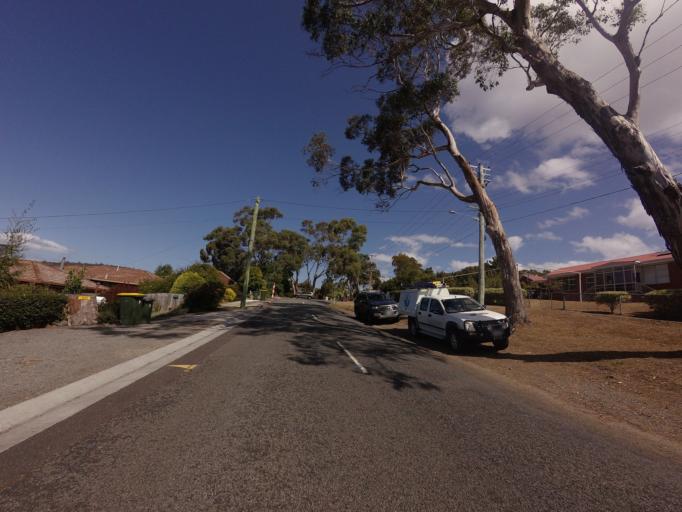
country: AU
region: Tasmania
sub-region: Hobart
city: Dynnyrne
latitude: -42.9131
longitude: 147.3236
